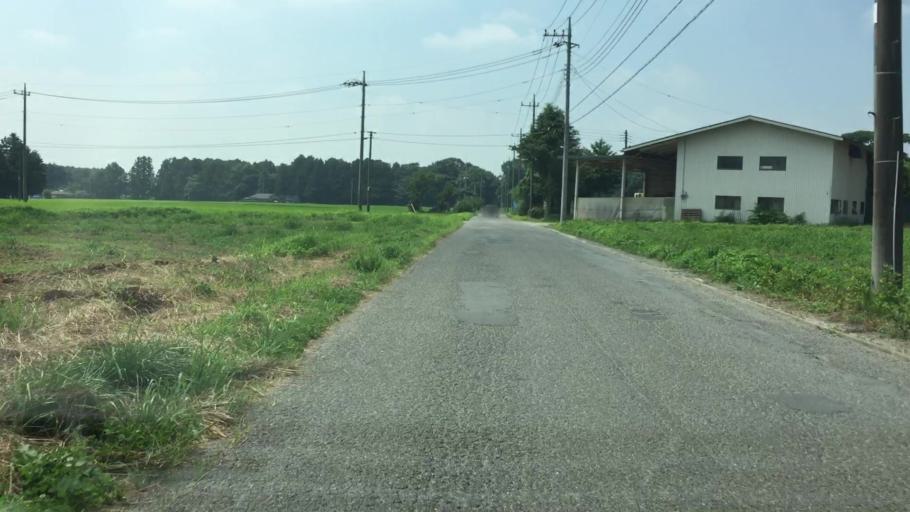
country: JP
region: Tochigi
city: Kuroiso
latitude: 36.9692
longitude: 139.9563
